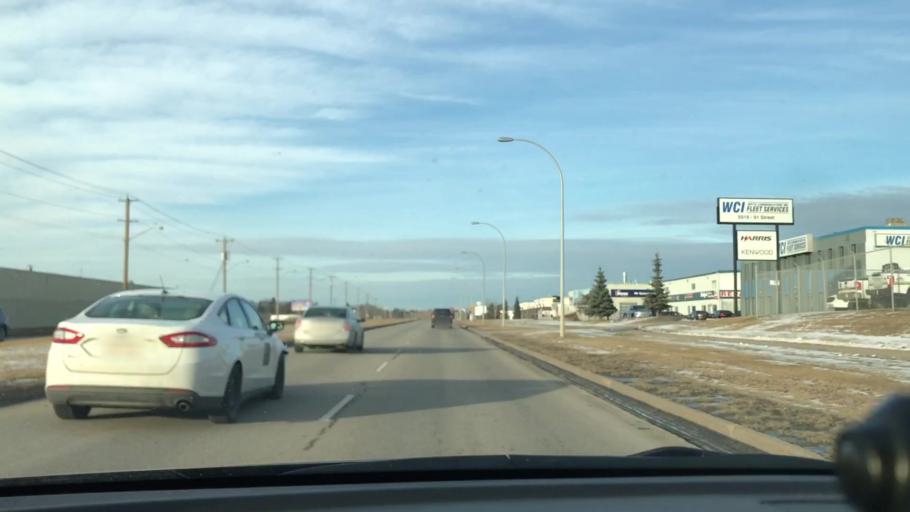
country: CA
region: Alberta
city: Edmonton
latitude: 53.4949
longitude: -113.4670
